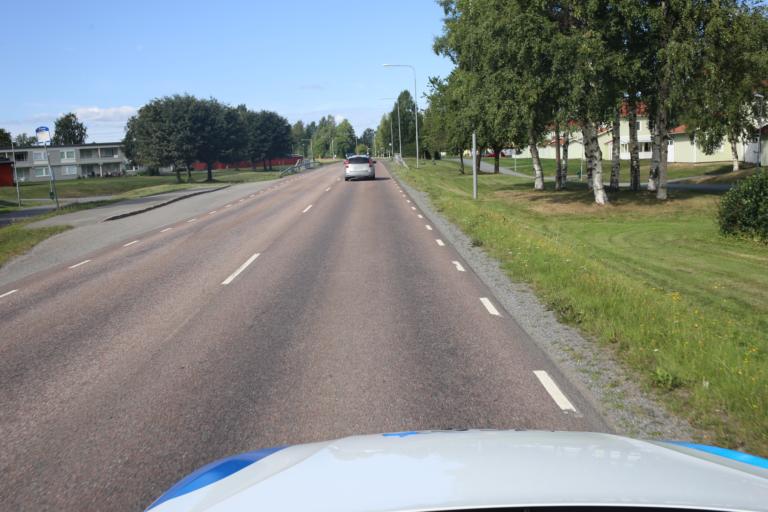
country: SE
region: Vaesterbotten
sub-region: Skelleftea Kommun
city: Skelleftea
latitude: 64.7451
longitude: 20.9798
